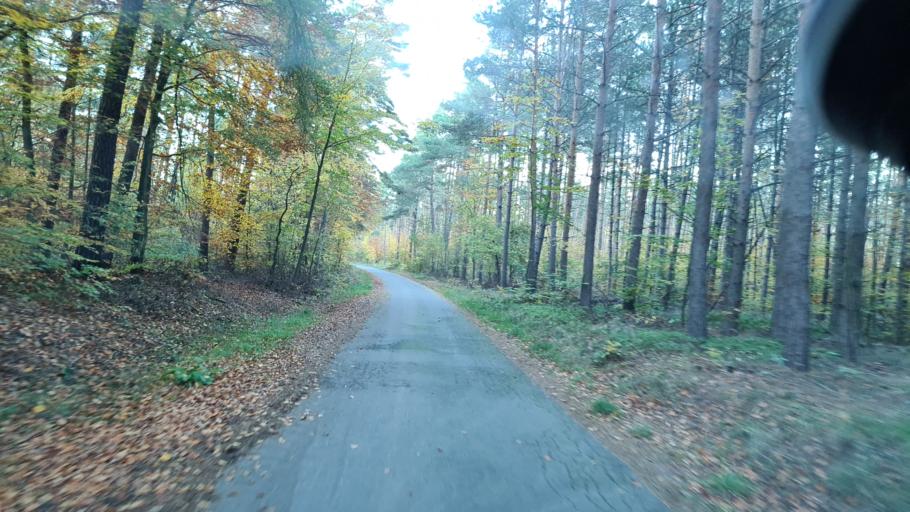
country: DE
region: Saxony
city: Belgern
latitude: 51.4372
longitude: 13.1147
